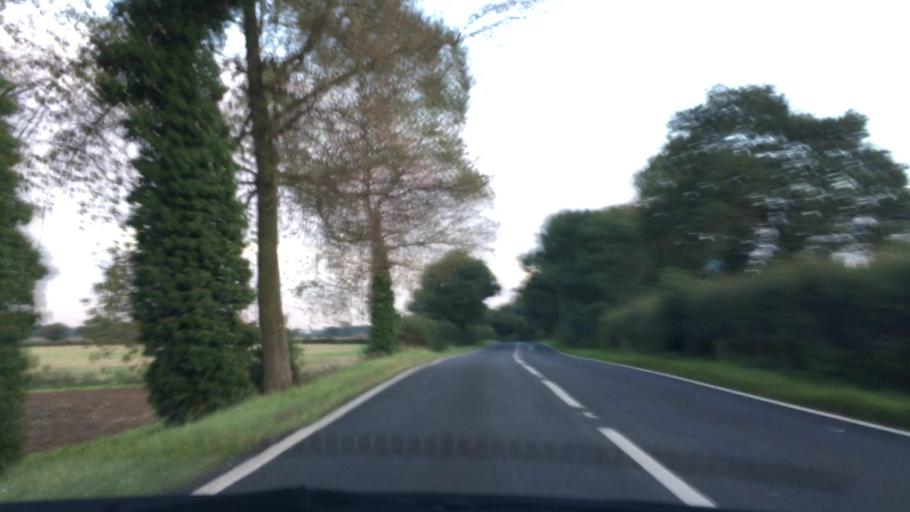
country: GB
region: England
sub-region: North East Lincolnshire
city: Wold Newton
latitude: 53.4645
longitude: -0.1011
